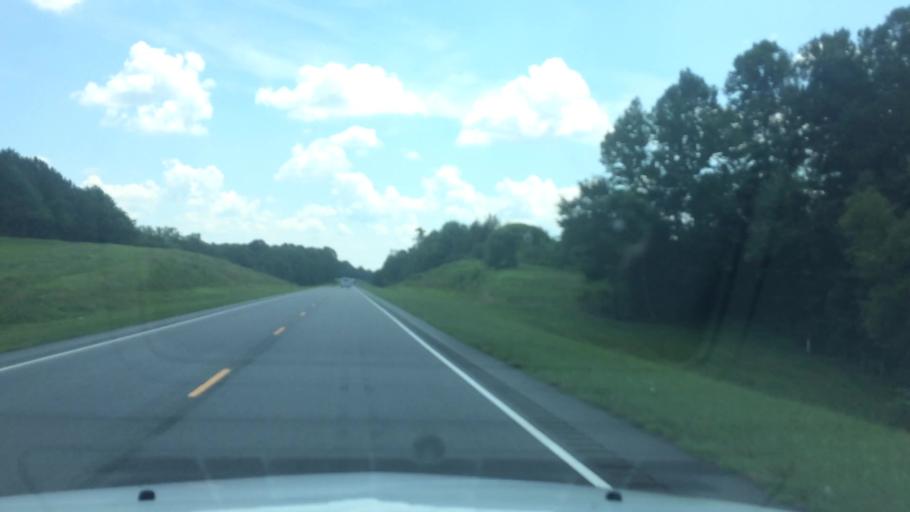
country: US
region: North Carolina
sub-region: Alexander County
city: Stony Point
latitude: 35.8777
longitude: -81.0702
